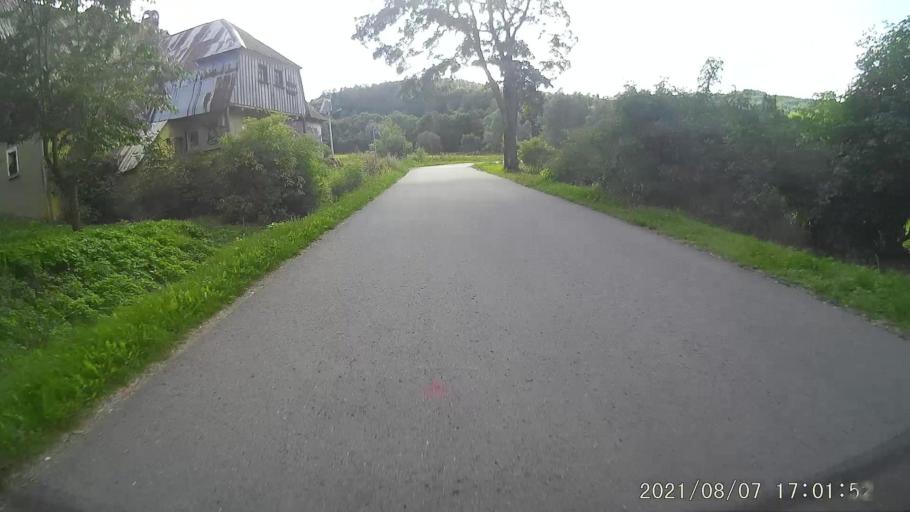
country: PL
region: Lower Silesian Voivodeship
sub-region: Powiat klodzki
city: Bystrzyca Klodzka
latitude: 50.2854
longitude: 16.5570
